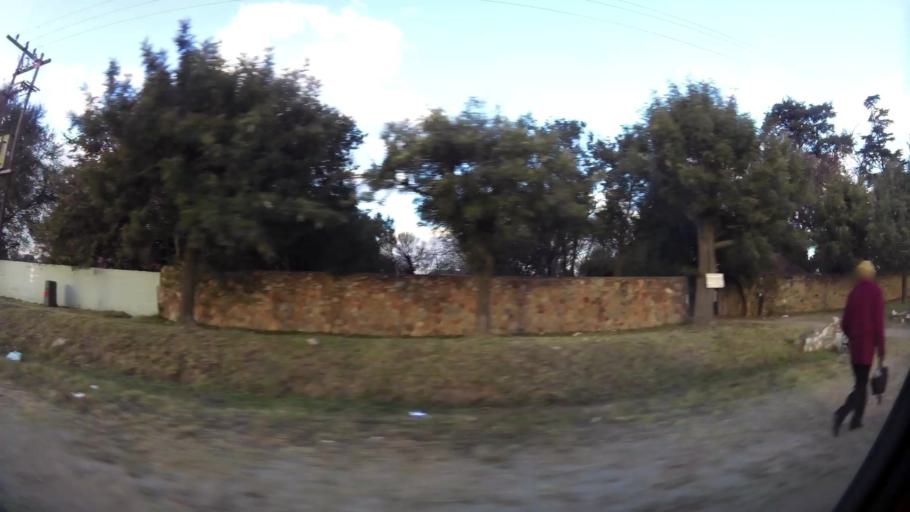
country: ZA
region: Gauteng
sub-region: City of Johannesburg Metropolitan Municipality
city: Midrand
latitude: -25.9860
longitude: 28.1528
